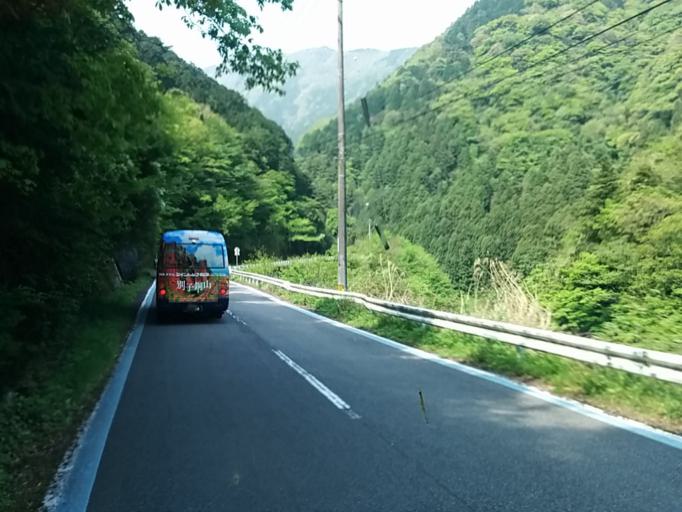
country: JP
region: Ehime
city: Niihama
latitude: 33.8838
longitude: 133.3033
